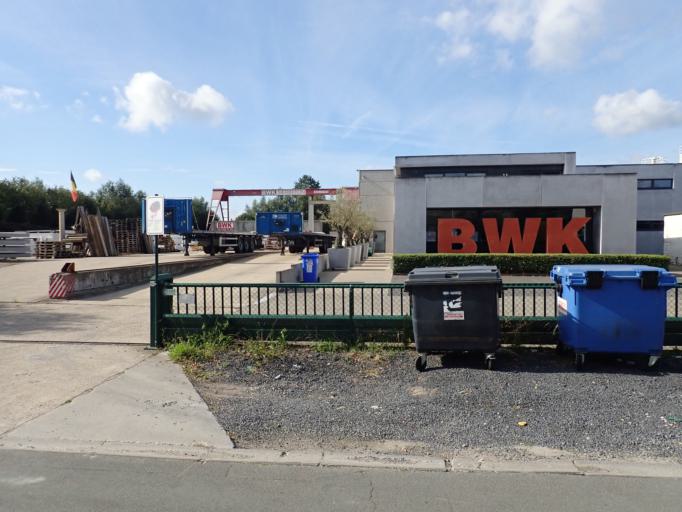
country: BE
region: Flanders
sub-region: Provincie Oost-Vlaanderen
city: Kruibeke
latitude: 51.1871
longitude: 4.3086
